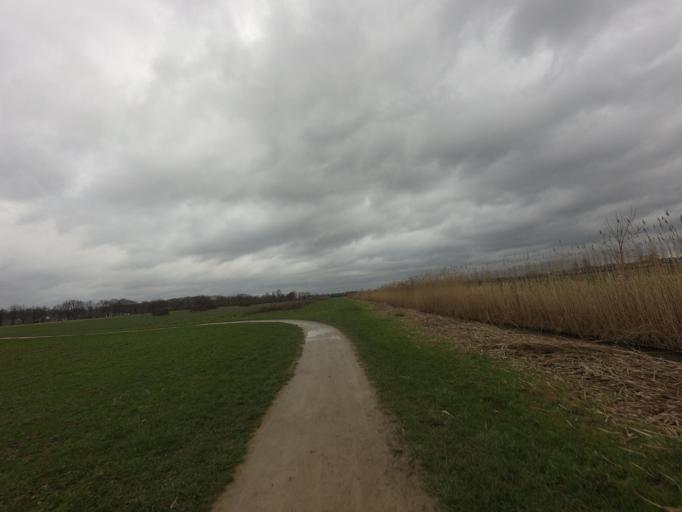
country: NL
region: Utrecht
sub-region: Stichtse Vecht
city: Spechtenkamp
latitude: 52.1123
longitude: 4.9975
